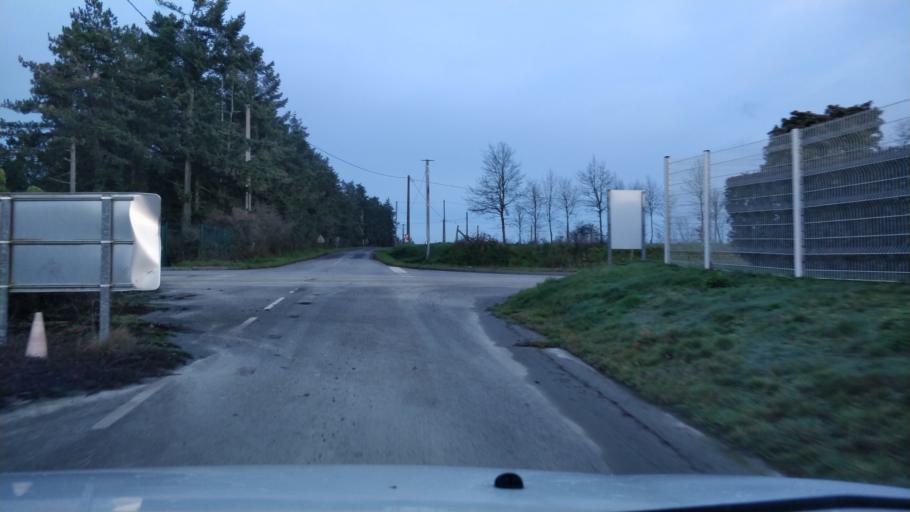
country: FR
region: Brittany
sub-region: Departement d'Ille-et-Vilaine
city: Louvigne-de-Bais
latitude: 48.0416
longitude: -1.3268
